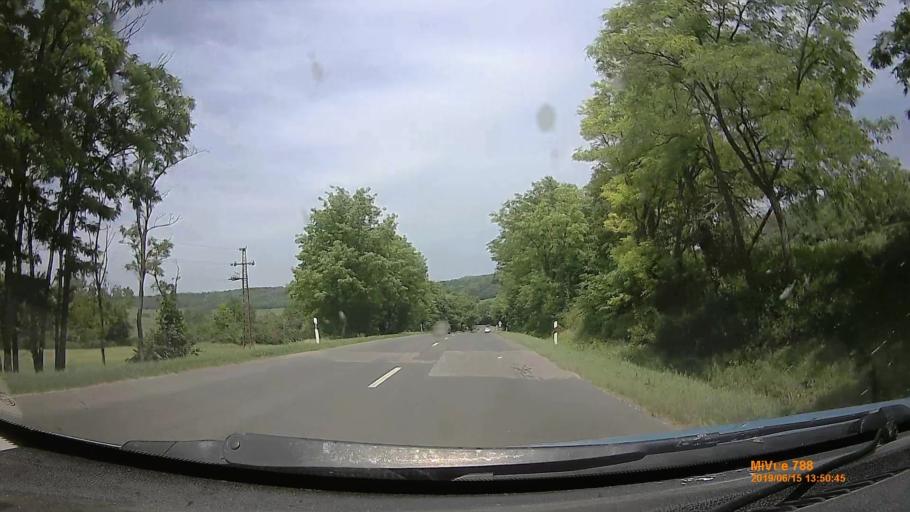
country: HU
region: Tolna
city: Iregszemcse
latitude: 46.7461
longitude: 18.1627
